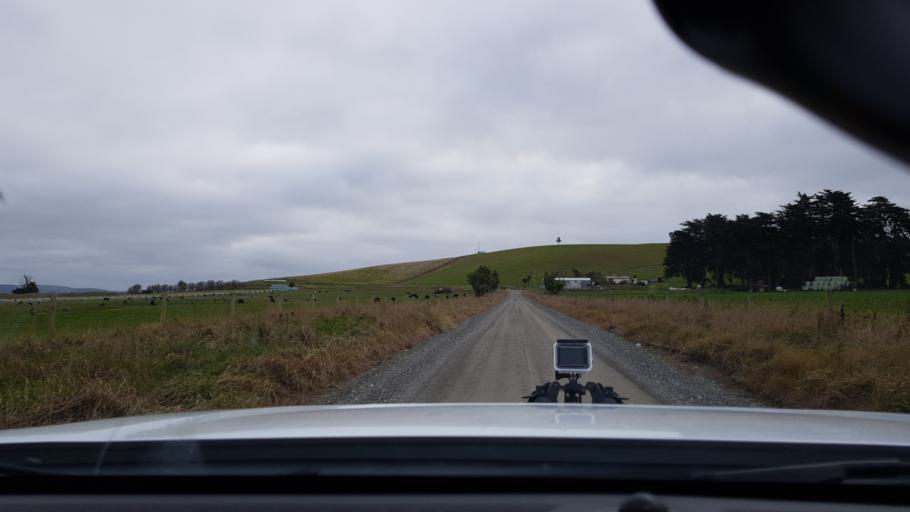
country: NZ
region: Otago
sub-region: Clutha District
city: Balclutha
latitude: -46.3232
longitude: 169.8554
